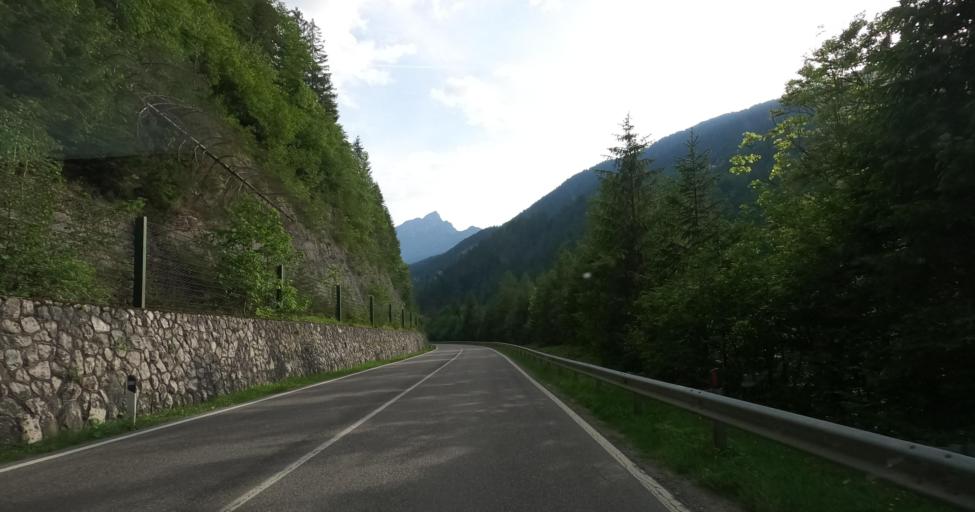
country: IT
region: Veneto
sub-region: Provincia di Belluno
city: Celat-San Tomaso Agordino
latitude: 46.3779
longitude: 11.9844
